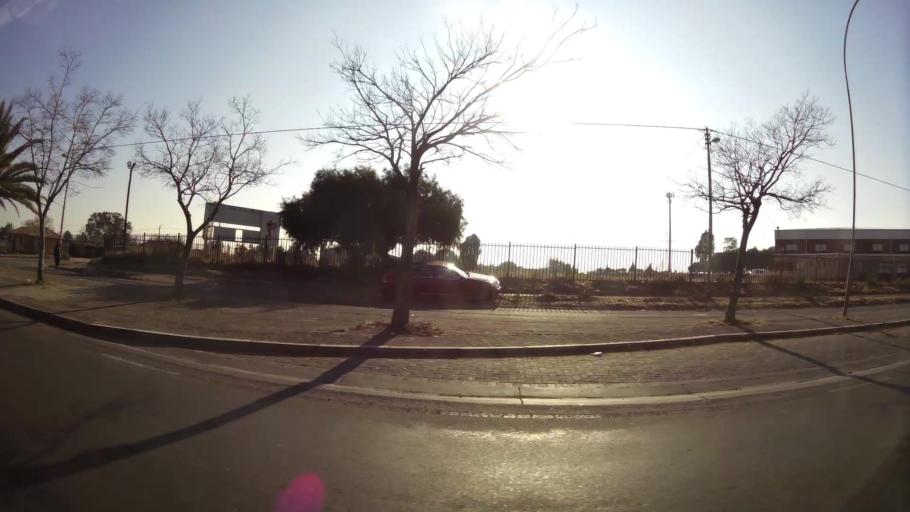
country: ZA
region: Orange Free State
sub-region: Mangaung Metropolitan Municipality
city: Bloemfontein
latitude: -29.1386
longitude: 26.2446
